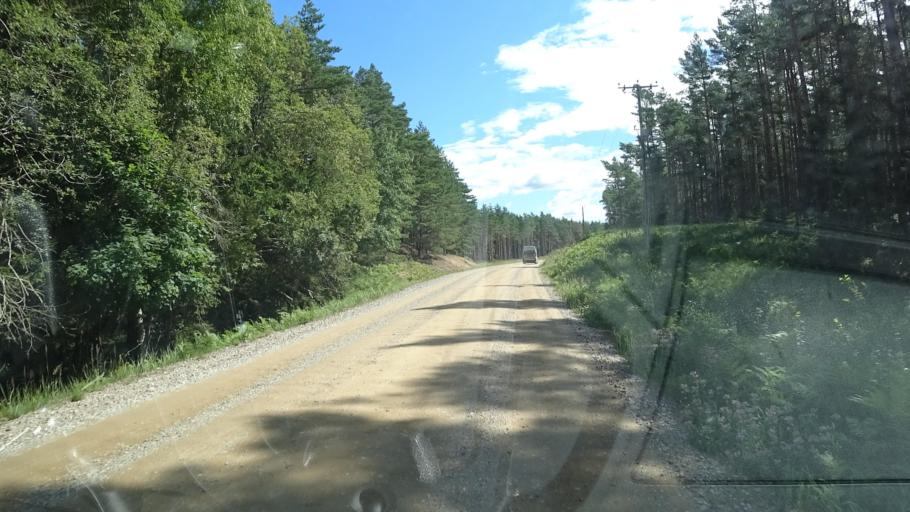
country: LV
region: Ventspils
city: Ventspils
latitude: 57.4886
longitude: 21.6640
